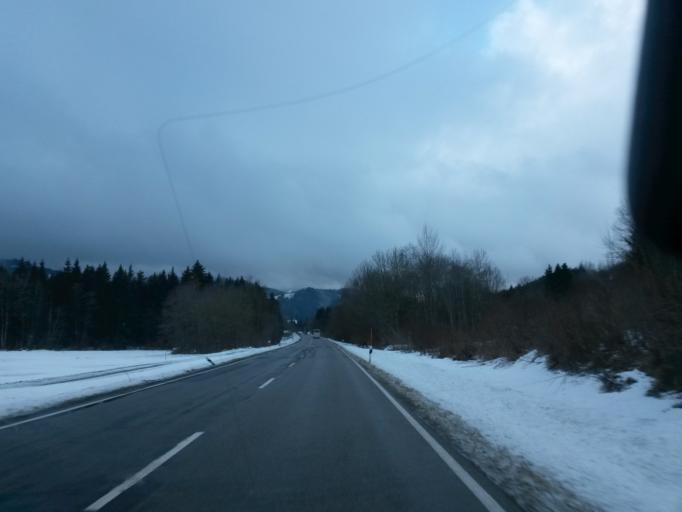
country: DE
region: Bavaria
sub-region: Swabia
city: Oy-Mittelberg
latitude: 47.6169
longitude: 10.4362
